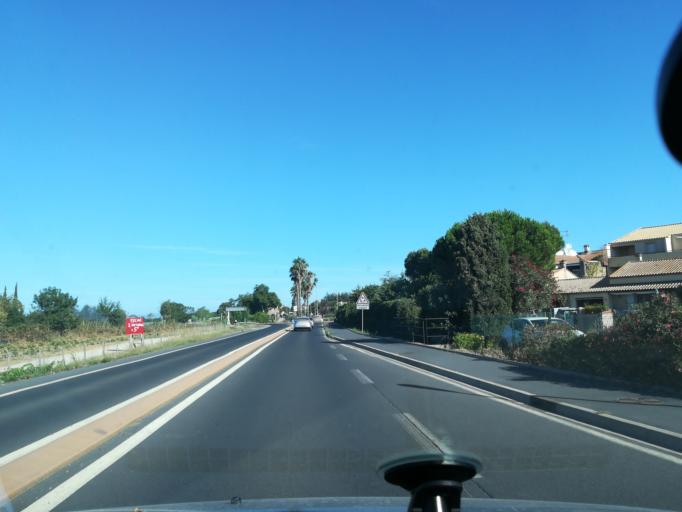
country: FR
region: Languedoc-Roussillon
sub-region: Departement de l'Herault
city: Portiragnes
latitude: 43.3028
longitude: 3.3323
